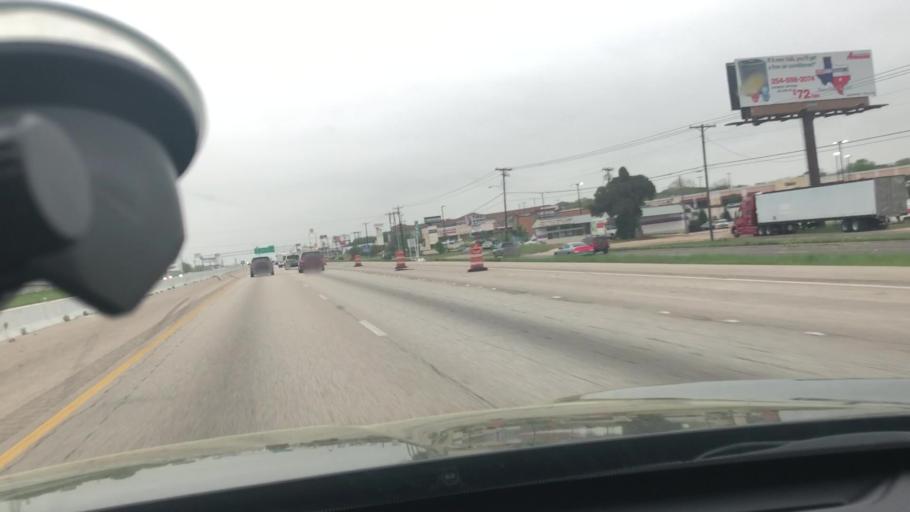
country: US
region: Texas
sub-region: Bell County
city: Temple
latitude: 31.0864
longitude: -97.4008
